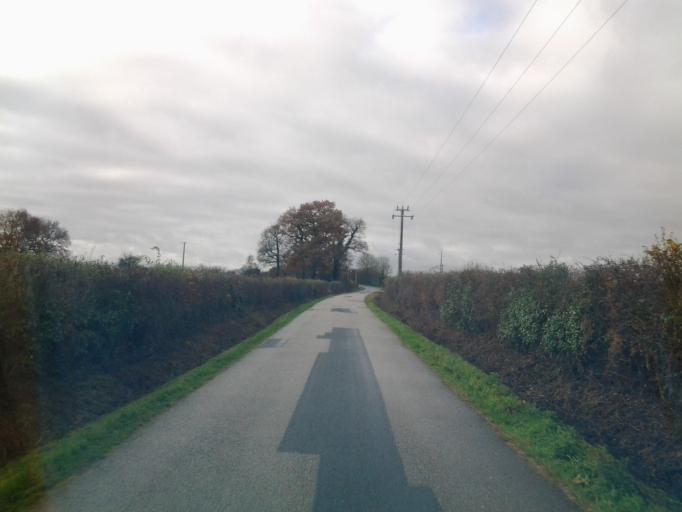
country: FR
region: Pays de la Loire
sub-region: Departement de la Vendee
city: Bournezeau
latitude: 46.6369
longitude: -1.1873
